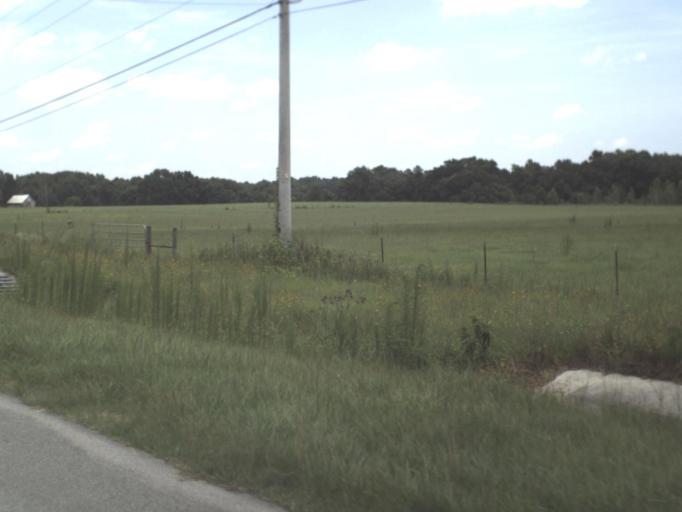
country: US
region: Florida
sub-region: Madison County
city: Madison
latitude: 30.4807
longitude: -83.4166
